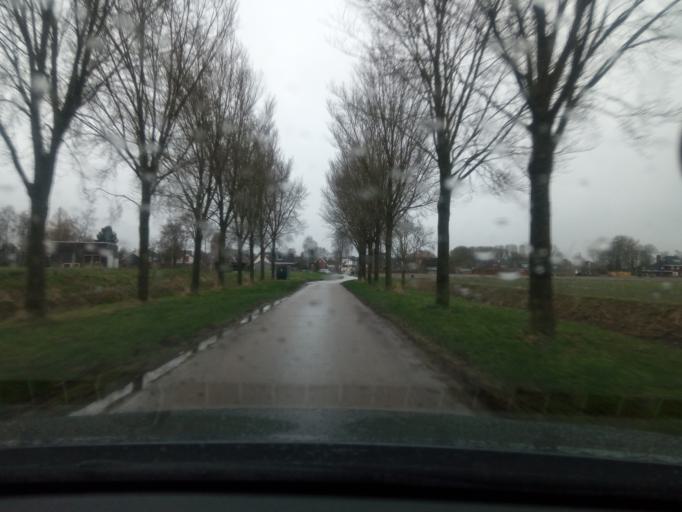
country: NL
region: Groningen
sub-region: Gemeente Appingedam
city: Appingedam
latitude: 53.3271
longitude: 6.7429
